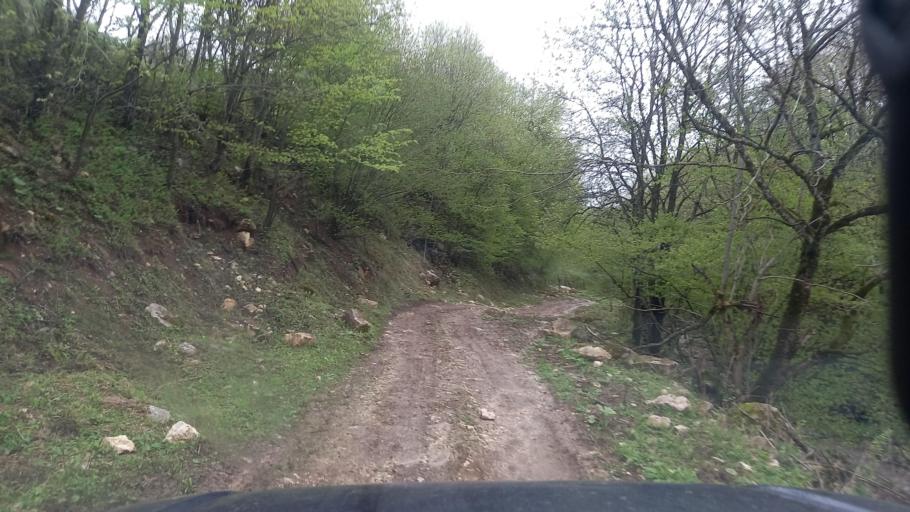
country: RU
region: Kabardino-Balkariya
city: Babugent
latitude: 43.2093
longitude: 43.5448
